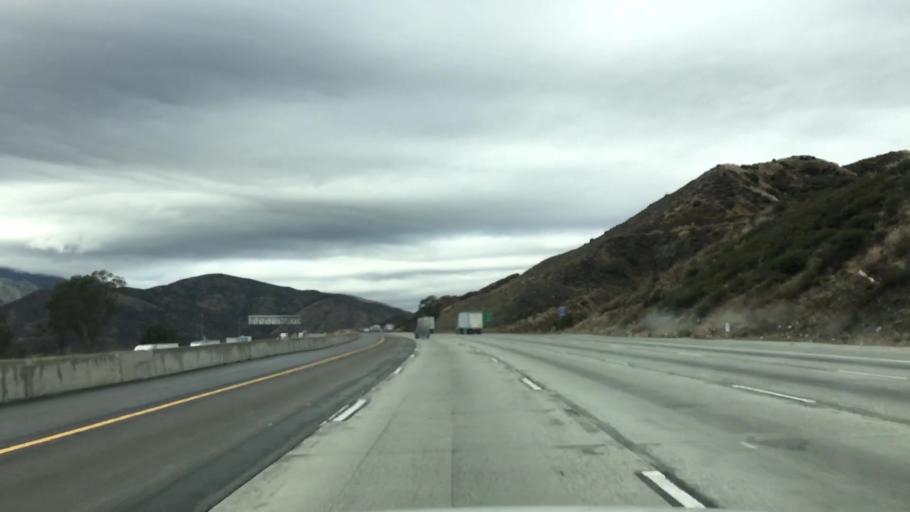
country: US
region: California
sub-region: San Bernardino County
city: Muscoy
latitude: 34.2478
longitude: -117.4384
